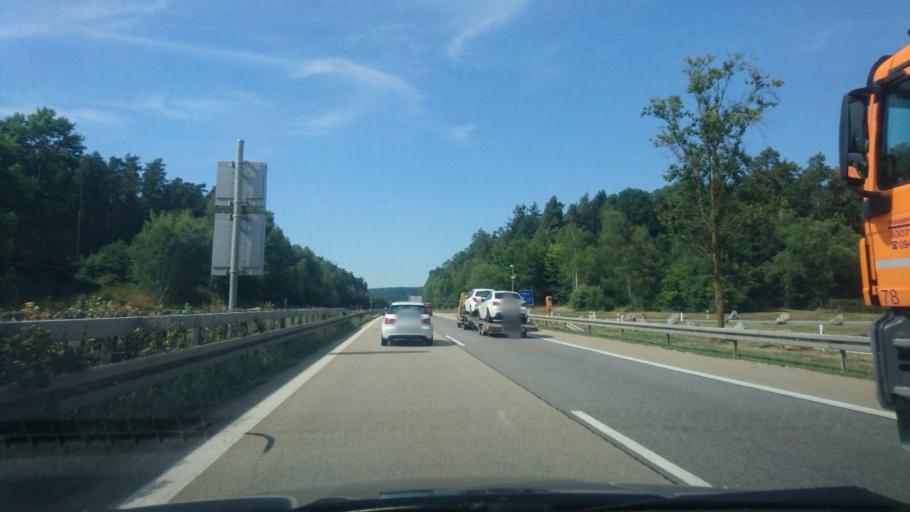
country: DE
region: Bavaria
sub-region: Upper Palatinate
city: Zeitlarn
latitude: 49.0888
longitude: 12.0973
